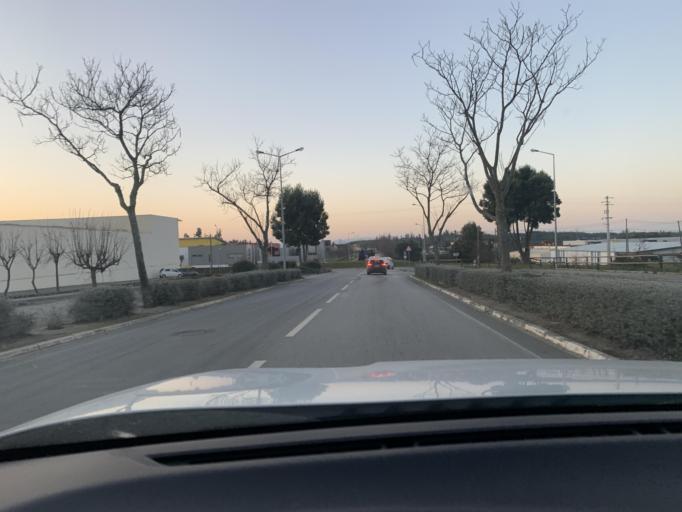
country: PT
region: Viseu
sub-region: Concelho de Tondela
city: Tondela
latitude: 40.4849
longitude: -8.0899
